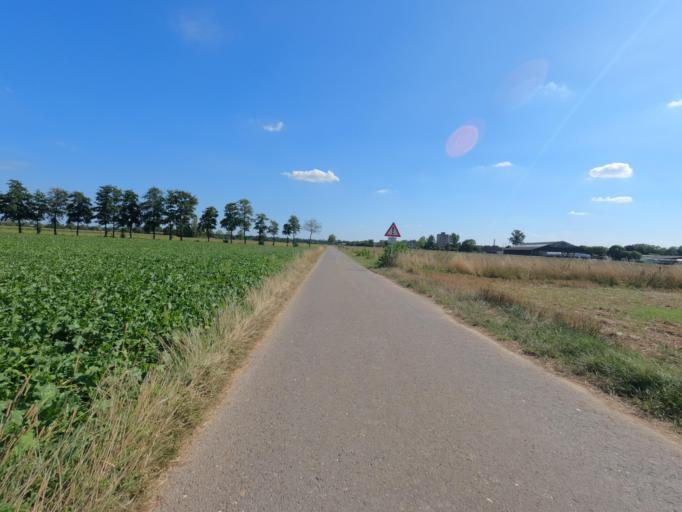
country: DE
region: North Rhine-Westphalia
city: Julich
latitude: 50.9350
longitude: 6.3256
